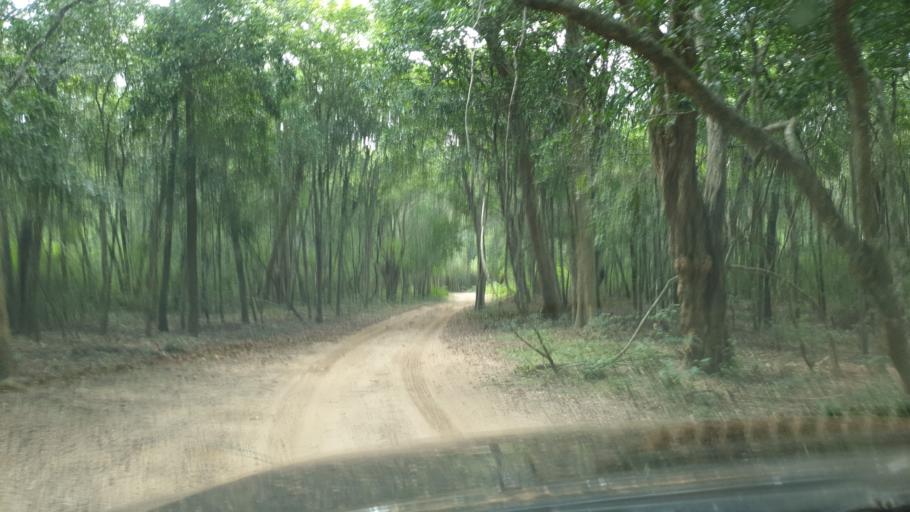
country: LK
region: North Central
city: Anuradhapura
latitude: 8.4200
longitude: 80.0116
